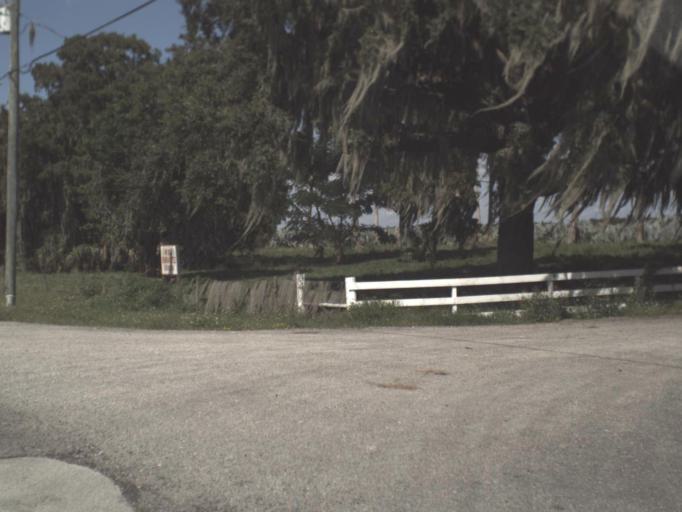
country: US
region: Florida
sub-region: Okeechobee County
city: Taylor Creek
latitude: 27.1657
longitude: -80.7175
